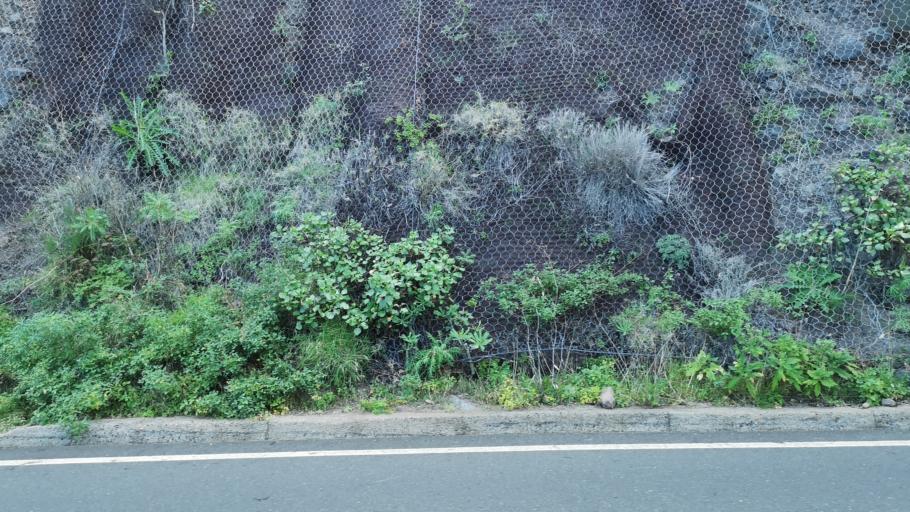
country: ES
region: Canary Islands
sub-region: Provincia de Santa Cruz de Tenerife
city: Agulo
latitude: 28.1854
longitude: -17.1926
